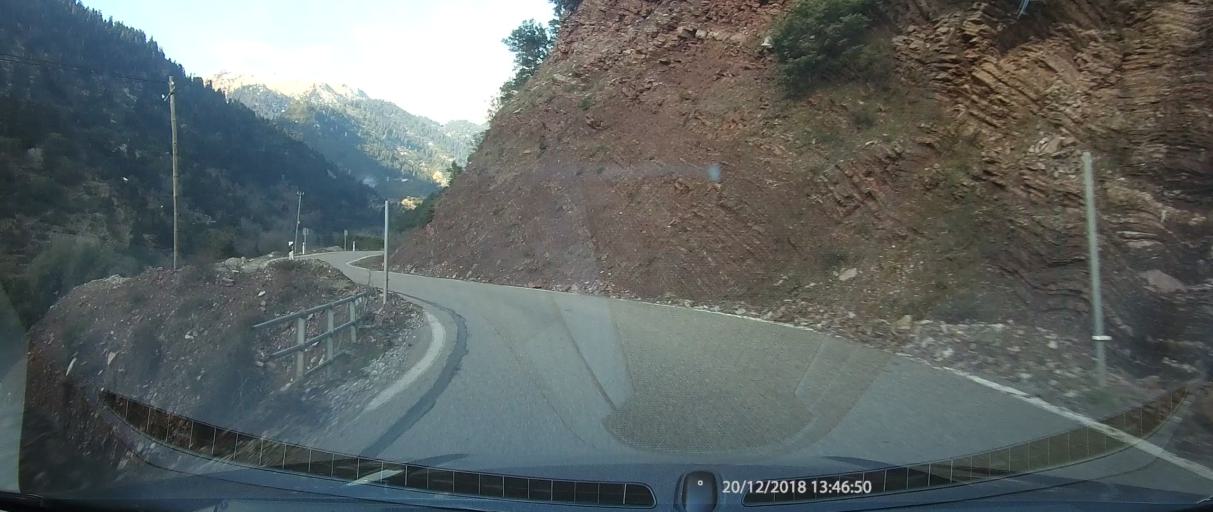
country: GR
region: West Greece
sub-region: Nomos Aitolias kai Akarnanias
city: Thermo
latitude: 38.6770
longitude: 21.6175
